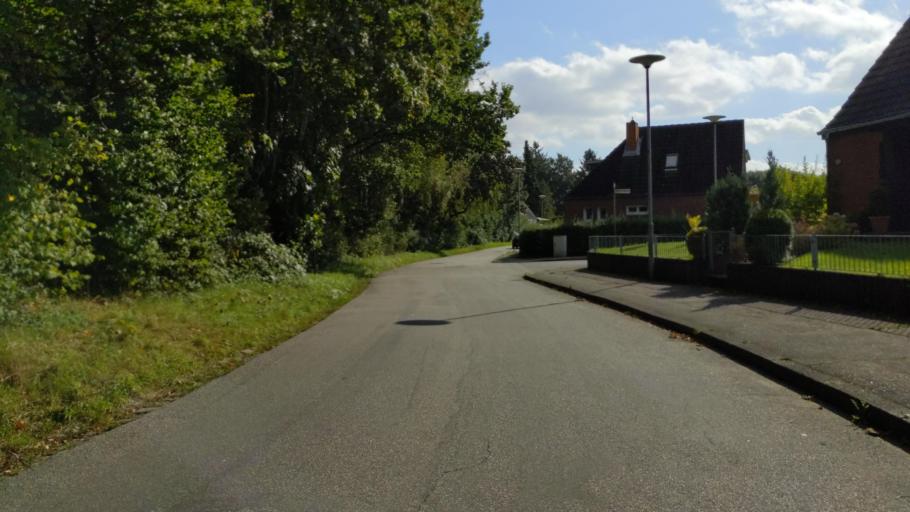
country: DE
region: Mecklenburg-Vorpommern
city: Selmsdorf
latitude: 53.9101
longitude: 10.7968
